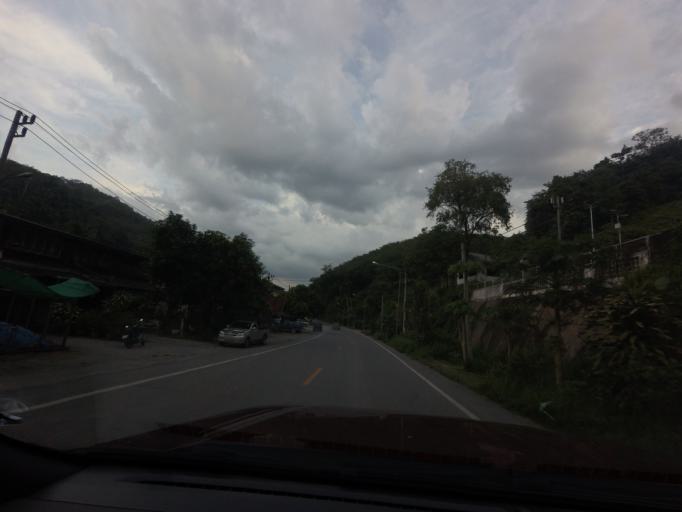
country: TH
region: Yala
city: Than To
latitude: 6.0077
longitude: 101.1944
